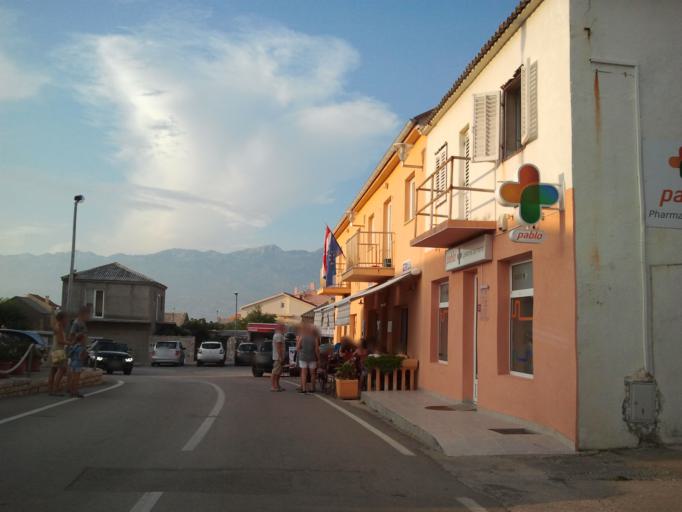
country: HR
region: Zadarska
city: Razanac
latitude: 44.2824
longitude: 15.3477
